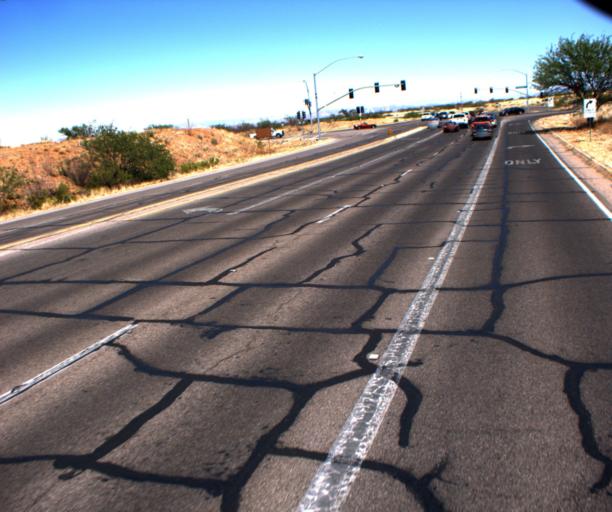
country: US
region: Arizona
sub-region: Cochise County
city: Sierra Vista
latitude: 31.5738
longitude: -110.3165
